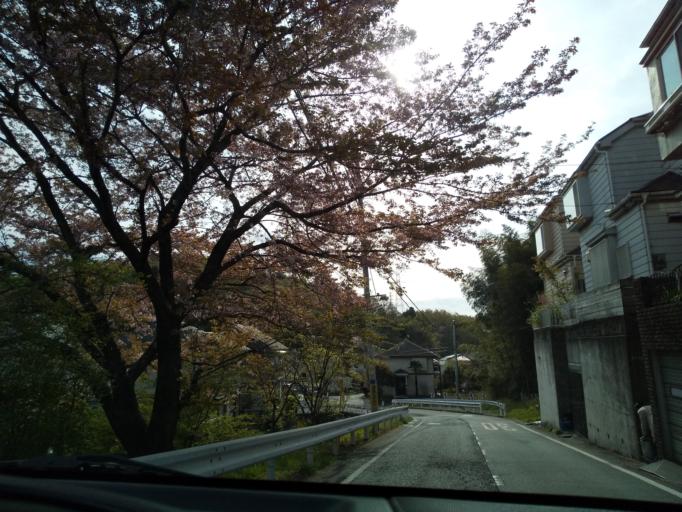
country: JP
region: Tokyo
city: Hino
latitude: 35.6495
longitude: 139.4253
